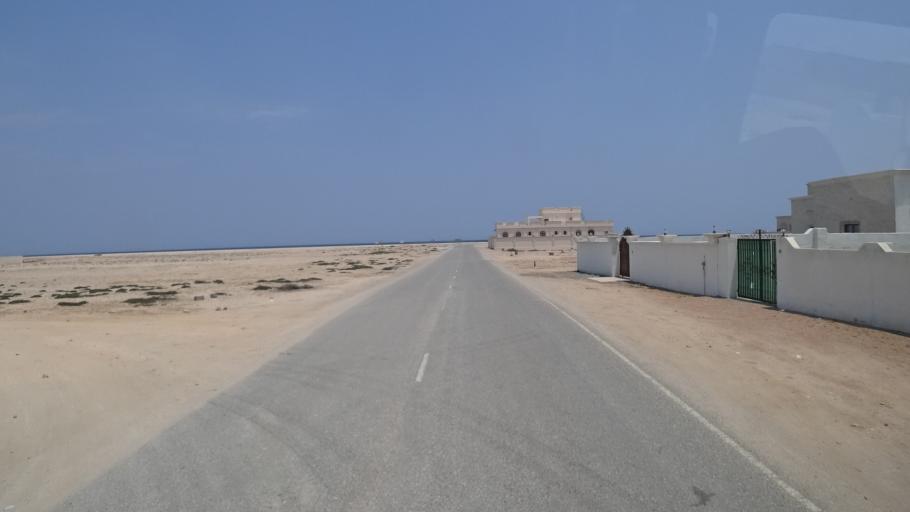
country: OM
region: Ash Sharqiyah
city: Sur
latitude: 22.5271
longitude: 59.7949
